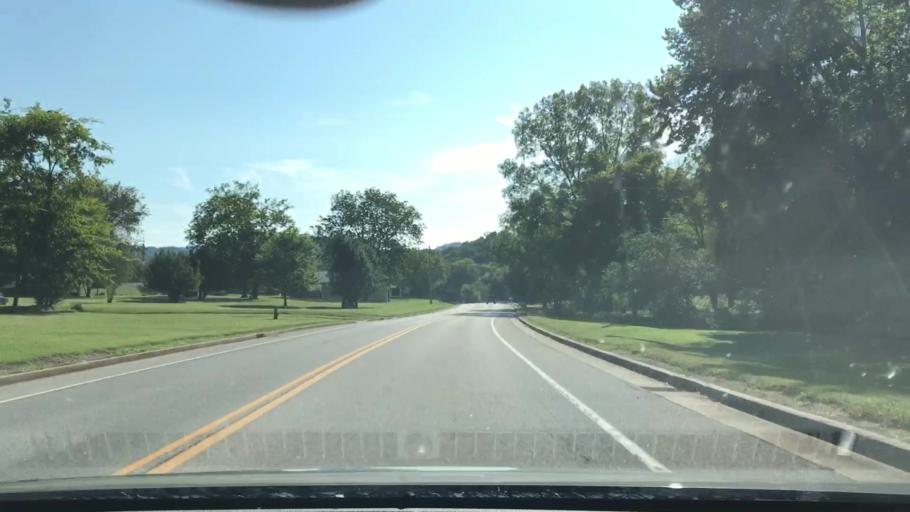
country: US
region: Tennessee
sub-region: Smith County
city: Carthage
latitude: 36.3198
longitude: -85.9174
